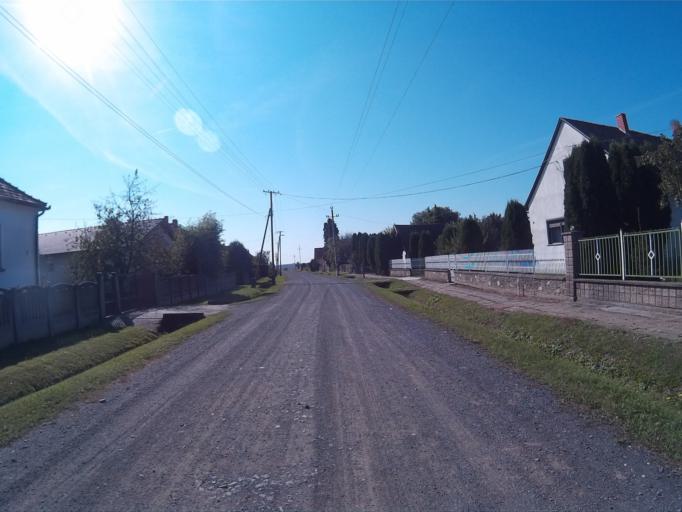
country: HU
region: Vas
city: Jak
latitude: 47.0854
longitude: 16.6279
